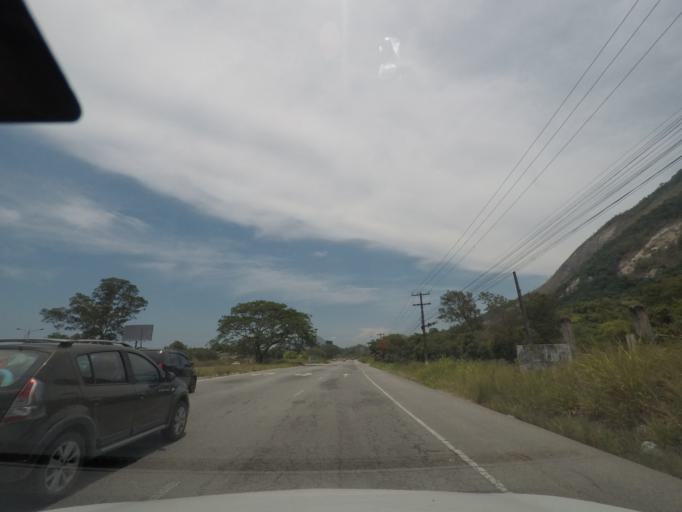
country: BR
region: Rio de Janeiro
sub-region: Marica
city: Marica
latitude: -22.9356
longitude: -42.9052
